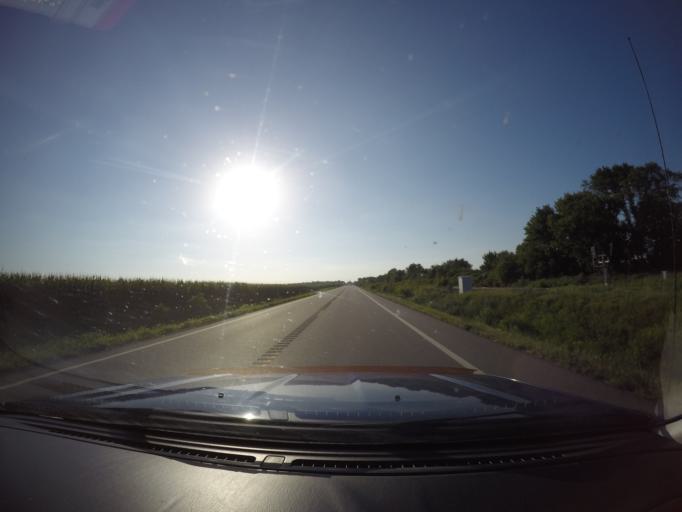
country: US
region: Kansas
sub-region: Shawnee County
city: Rossville
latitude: 39.1265
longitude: -95.9337
